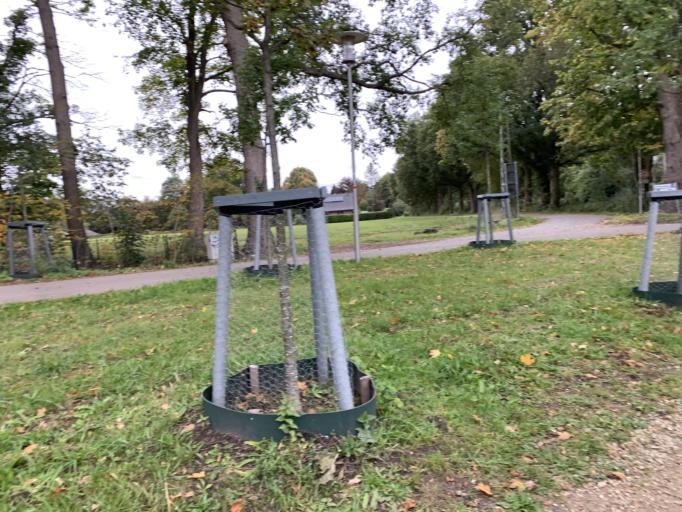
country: DE
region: North Rhine-Westphalia
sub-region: Regierungsbezirk Munster
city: Rheine
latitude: 52.3002
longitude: 7.4194
